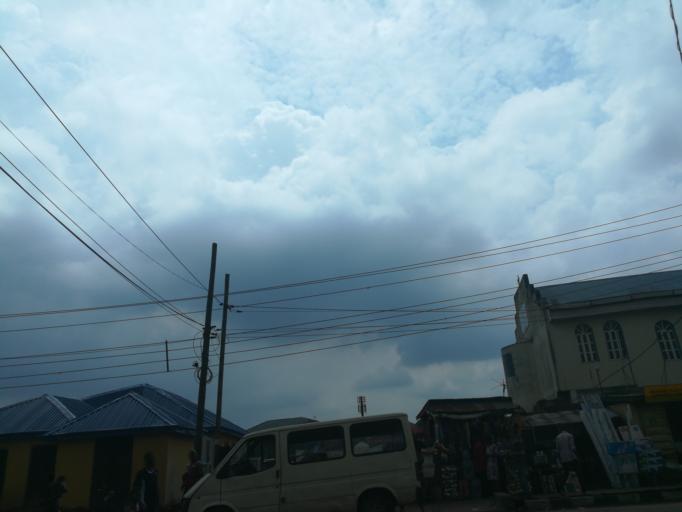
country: NG
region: Lagos
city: Ojota
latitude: 6.5907
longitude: 3.3743
